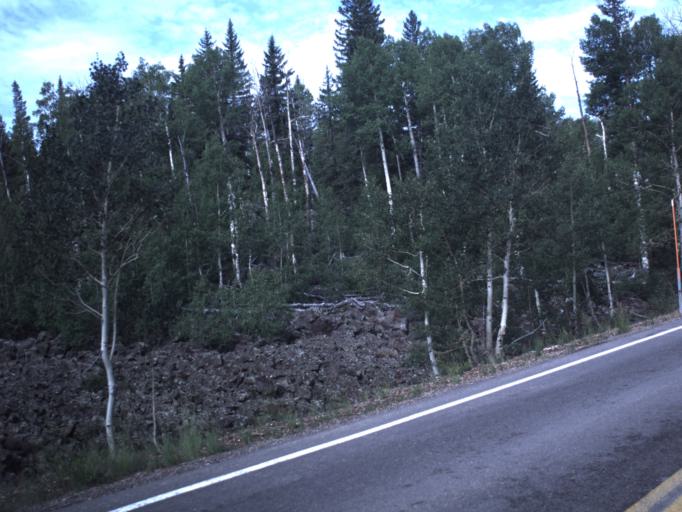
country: US
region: Utah
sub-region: Iron County
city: Parowan
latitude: 37.5238
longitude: -112.7410
